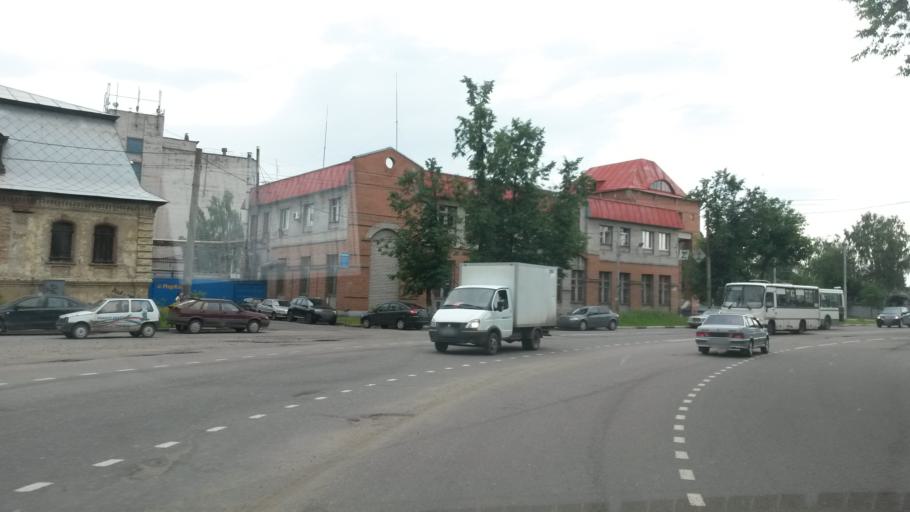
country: RU
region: Jaroslavl
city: Yaroslavl
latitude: 57.6079
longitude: 39.8430
